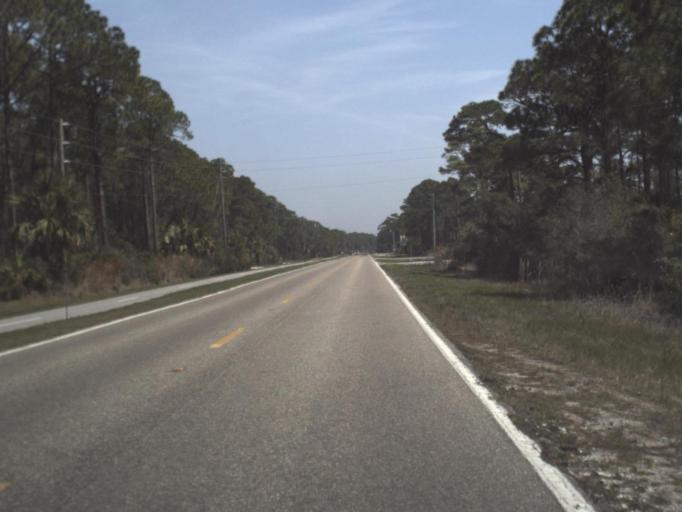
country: US
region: Florida
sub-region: Gulf County
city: Port Saint Joe
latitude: 29.6820
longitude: -85.3345
